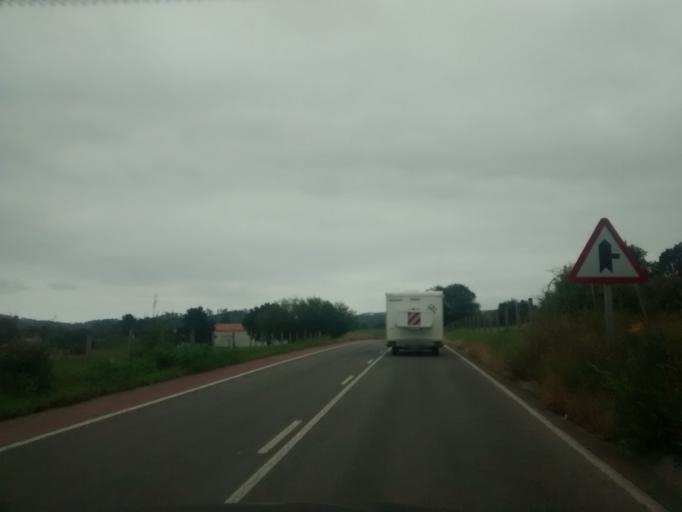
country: ES
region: Cantabria
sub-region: Provincia de Cantabria
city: Luzmela
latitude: 43.3082
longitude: -4.1984
